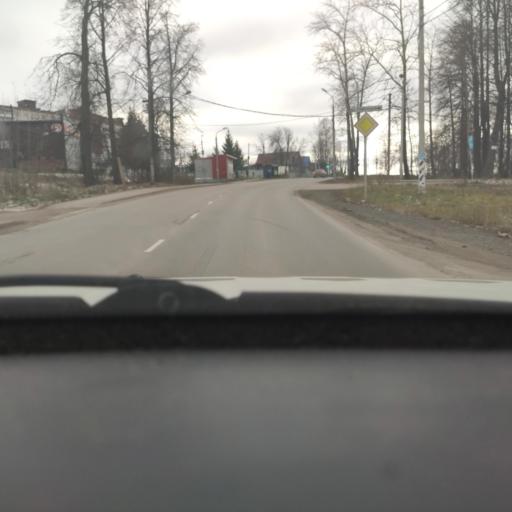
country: RU
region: Perm
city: Perm
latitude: 58.0894
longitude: 56.4026
